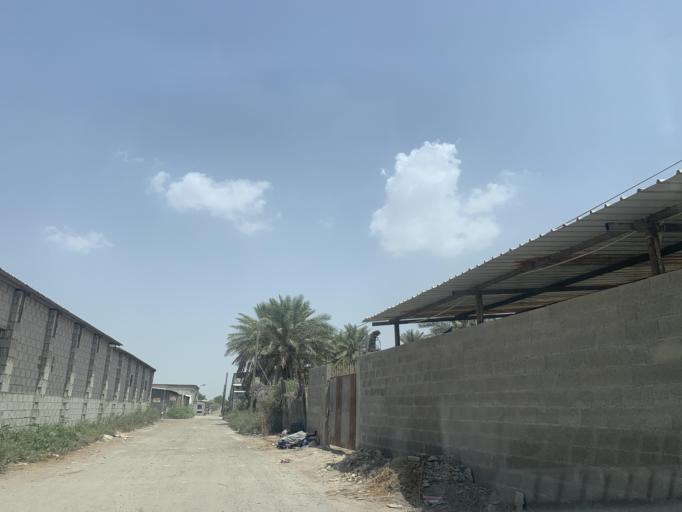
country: BH
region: Central Governorate
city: Madinat Hamad
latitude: 26.1620
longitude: 50.4944
